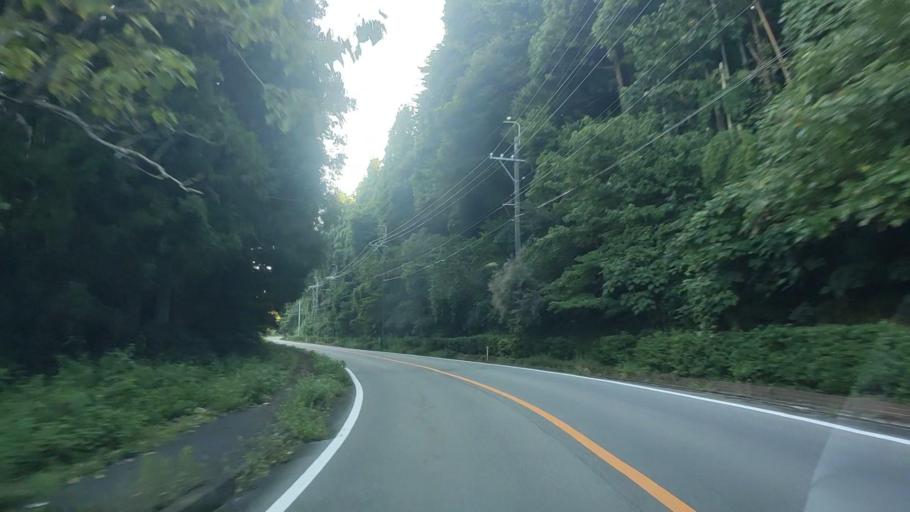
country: JP
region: Ishikawa
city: Nanao
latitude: 37.1053
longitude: 136.9773
